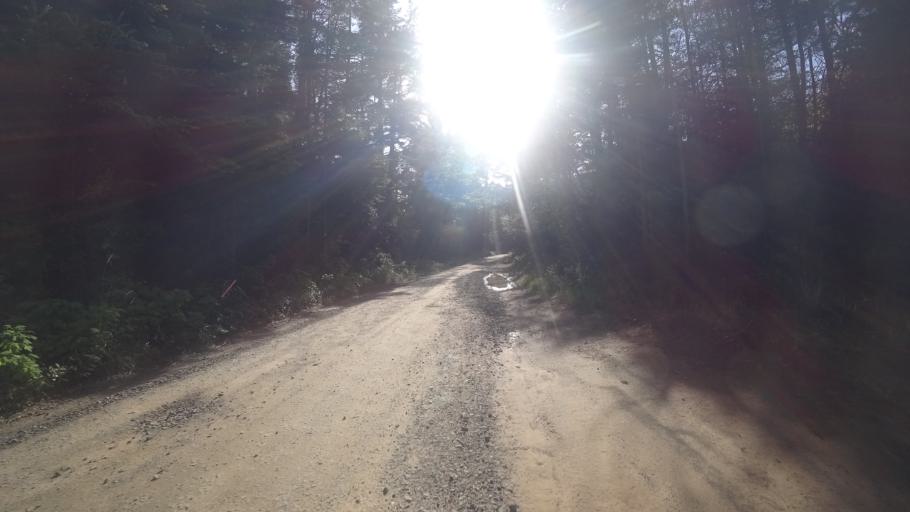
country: US
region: Oregon
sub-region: Douglas County
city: Reedsport
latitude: 43.7474
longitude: -124.1639
